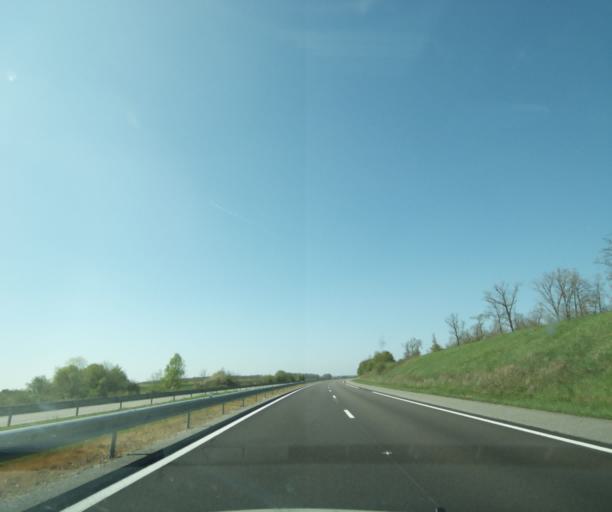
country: FR
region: Centre
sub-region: Departement du Loiret
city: Ouzouer-sur-Trezee
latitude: 47.6220
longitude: 2.7971
